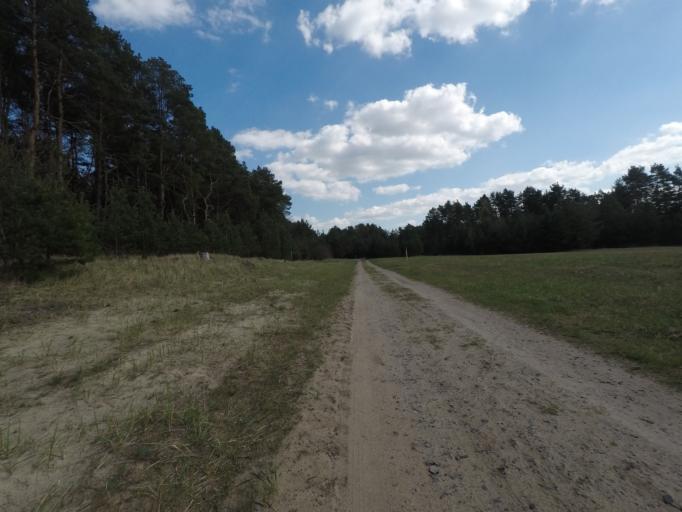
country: DE
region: Brandenburg
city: Melchow
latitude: 52.8320
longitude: 13.7135
